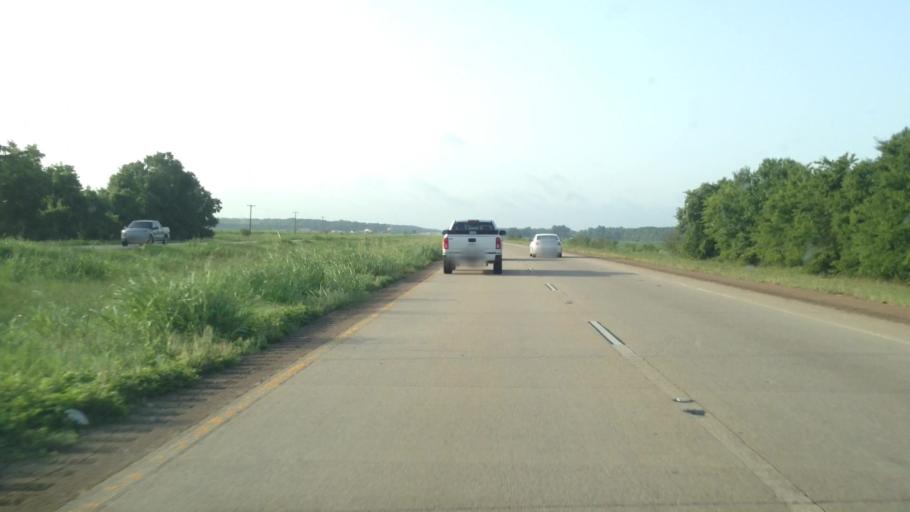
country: US
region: Louisiana
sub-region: Rapides Parish
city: Woodworth
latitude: 31.1859
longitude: -92.4718
